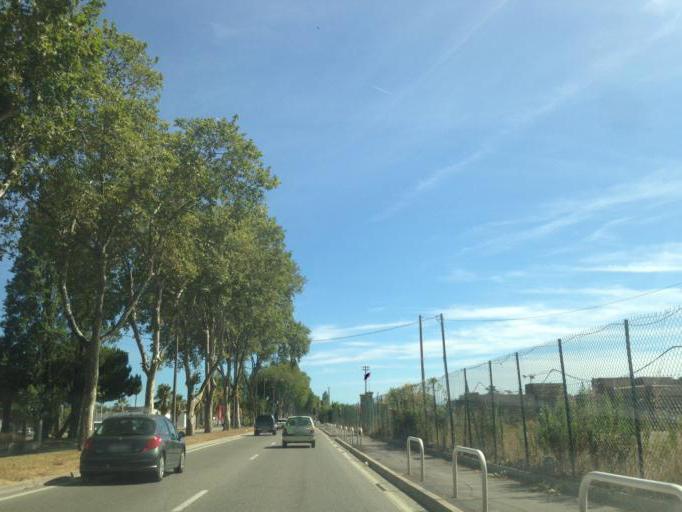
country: FR
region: Provence-Alpes-Cote d'Azur
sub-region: Departement des Alpes-Maritimes
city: Saint-Laurent-du-Var
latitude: 43.6891
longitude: 7.1964
